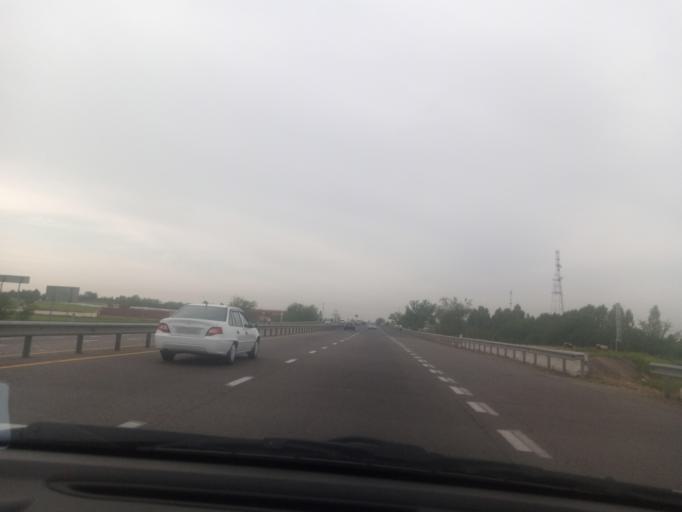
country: UZ
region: Toshkent
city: Tuytepa
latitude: 41.1255
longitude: 69.4382
